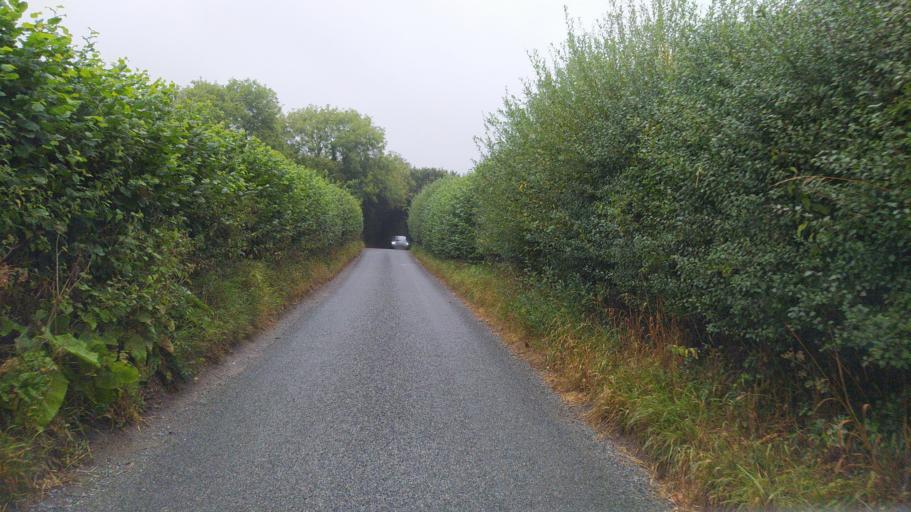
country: GB
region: England
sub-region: Wiltshire
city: Ansty
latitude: 51.0050
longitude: -2.1139
